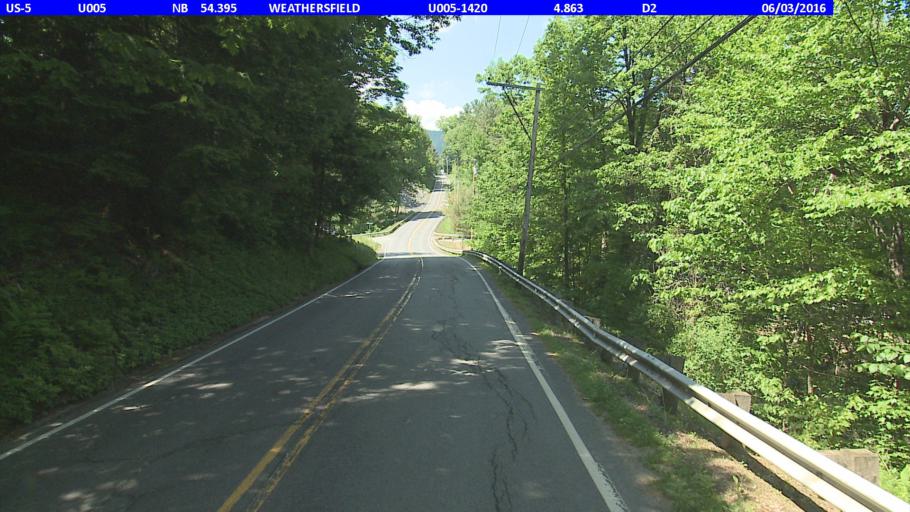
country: US
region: New Hampshire
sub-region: Sullivan County
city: Claremont
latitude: 43.4024
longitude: -72.4060
